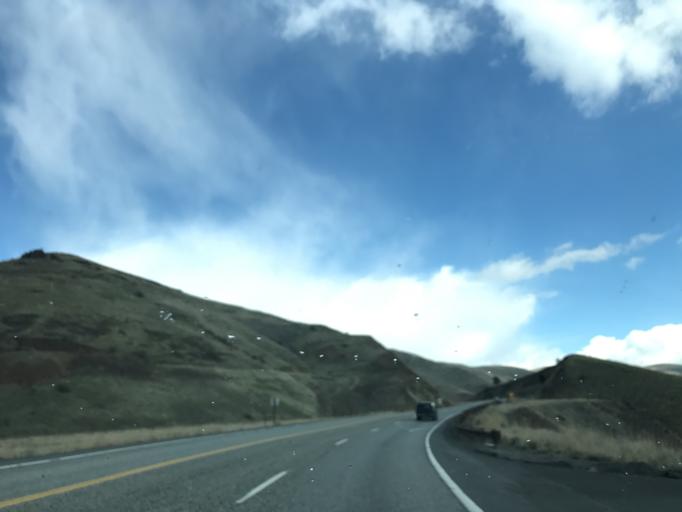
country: US
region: Idaho
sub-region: Idaho County
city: Grangeville
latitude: 45.7866
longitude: -116.2928
